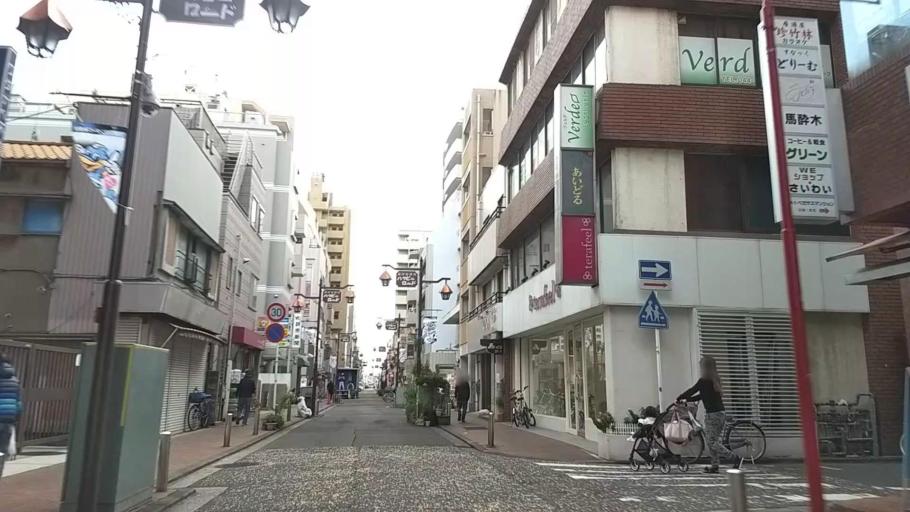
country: JP
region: Kanagawa
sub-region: Kawasaki-shi
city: Kawasaki
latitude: 35.5329
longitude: 139.6920
